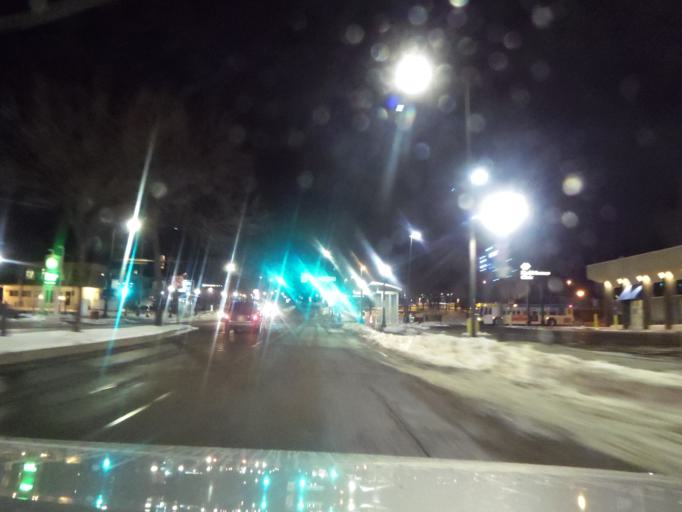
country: US
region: Minnesota
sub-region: Dakota County
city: Mendota Heights
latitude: 44.9179
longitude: -93.1856
